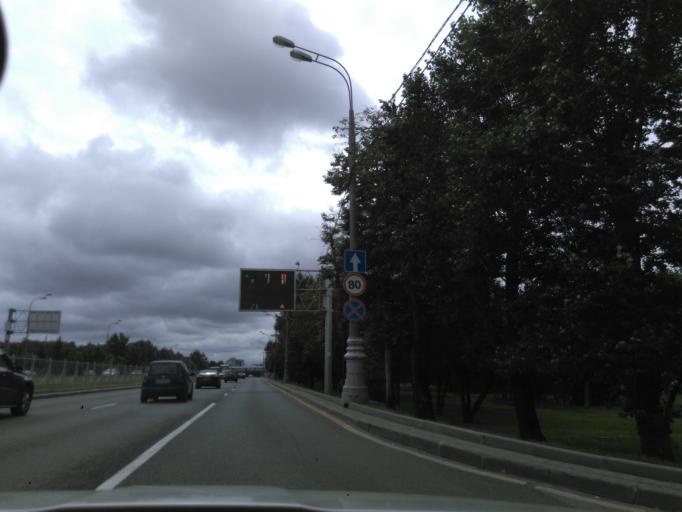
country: RU
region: Moskovskaya
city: Bol'shaya Setun'
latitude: 55.7391
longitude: 37.4339
